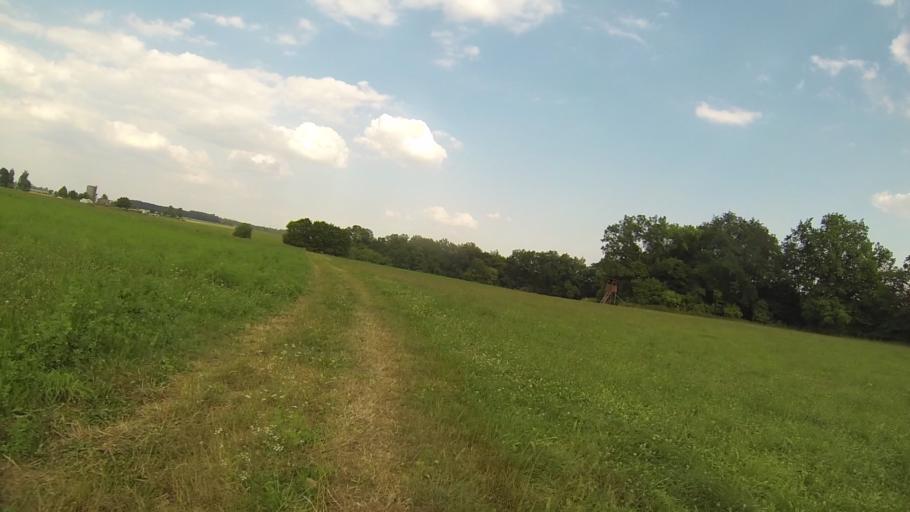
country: DE
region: Baden-Wuerttemberg
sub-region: Tuebingen Region
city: Blaubeuren
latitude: 48.4529
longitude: 9.8490
